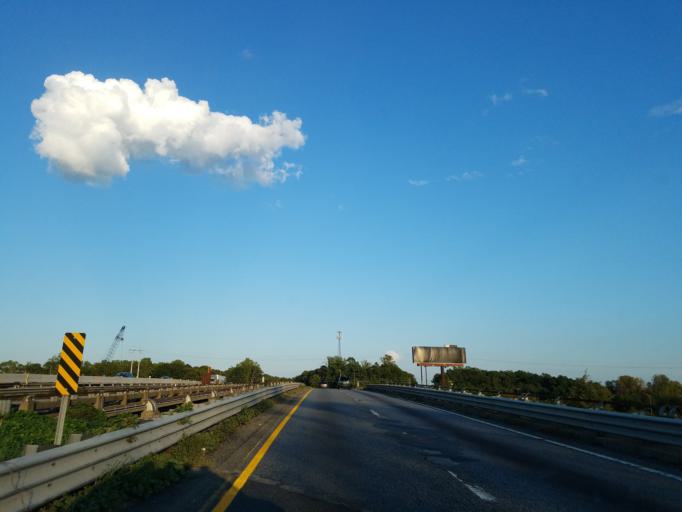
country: US
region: South Carolina
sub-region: Cherokee County
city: Blacksburg
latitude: 35.1598
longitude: -81.4680
